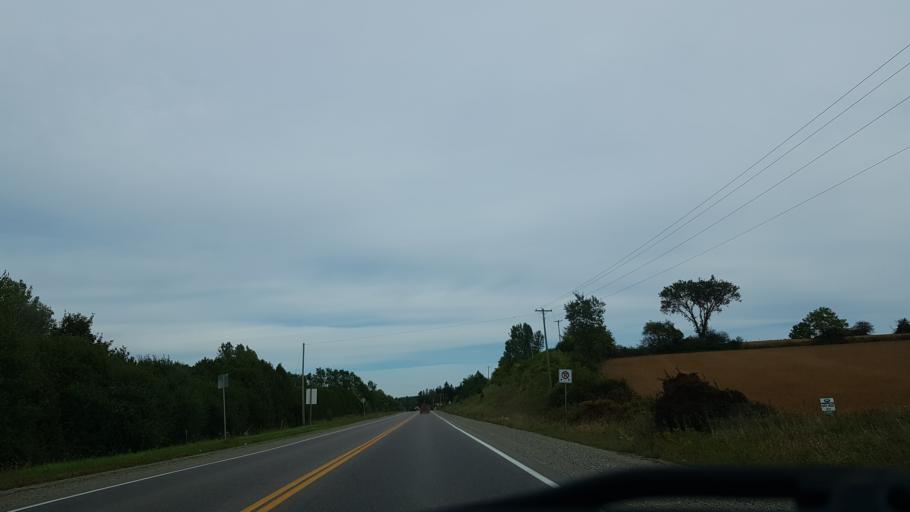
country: CA
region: Ontario
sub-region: Wellington County
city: Guelph
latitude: 43.6039
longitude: -80.2295
